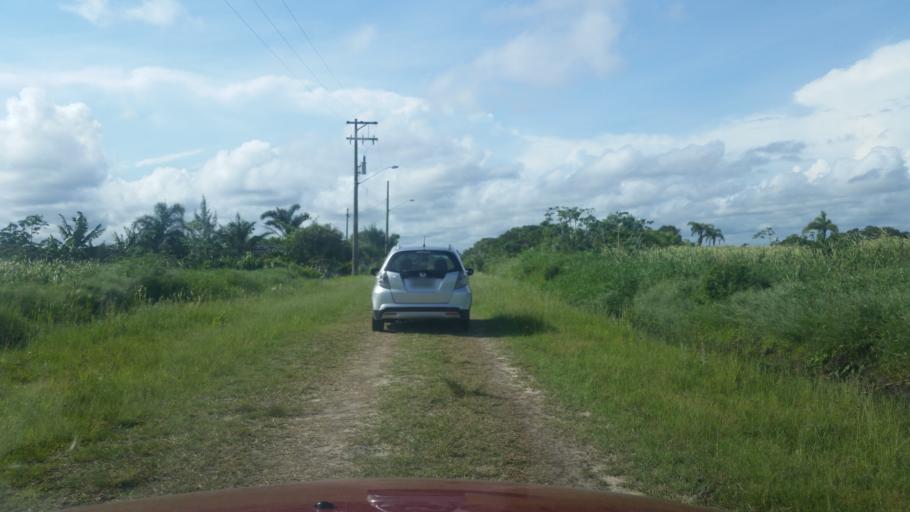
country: BR
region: Sao Paulo
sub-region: Iguape
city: Iguape
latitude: -24.7691
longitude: -47.5892
